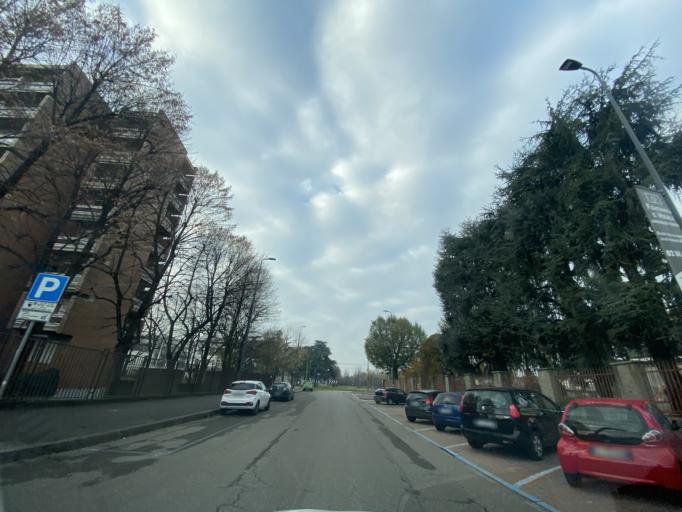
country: IT
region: Lombardy
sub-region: Citta metropolitana di Milano
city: Bresso
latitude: 45.5112
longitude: 9.1919
